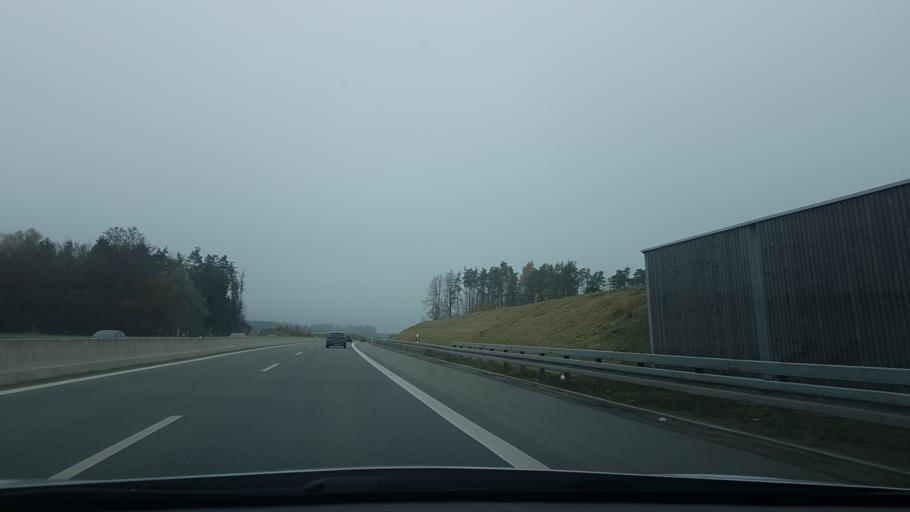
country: DE
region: Bavaria
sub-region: Lower Bavaria
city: Ergoldsbach
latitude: 48.6940
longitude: 12.1802
